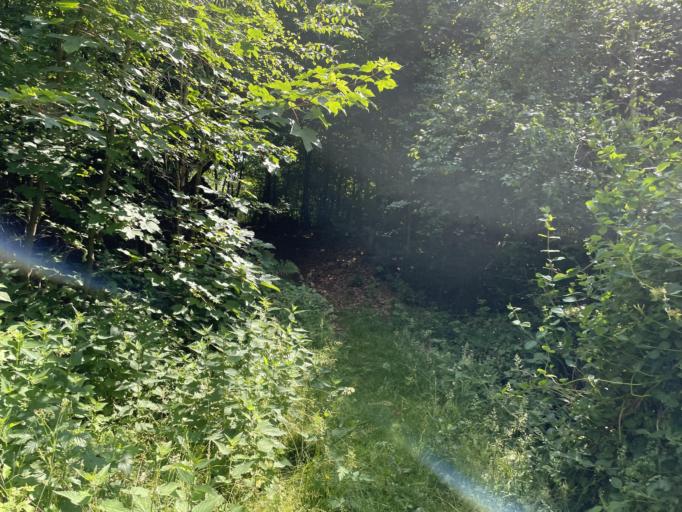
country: DE
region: Schleswig-Holstein
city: Mildstedt
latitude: 54.4708
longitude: 9.1107
